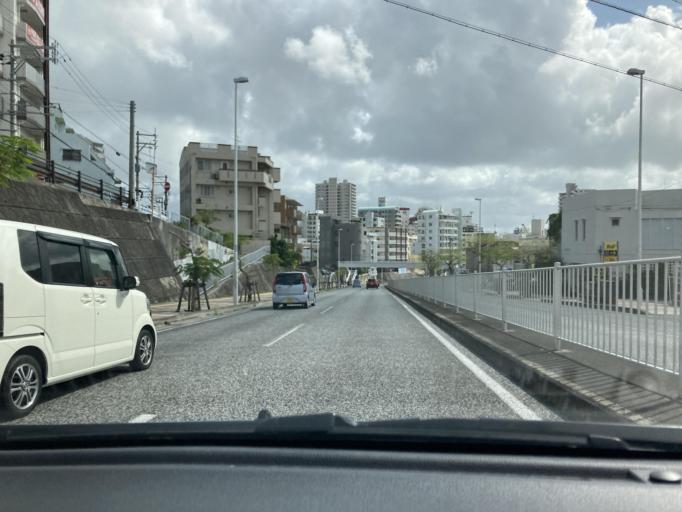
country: JP
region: Okinawa
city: Naha-shi
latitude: 26.2224
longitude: 127.6925
